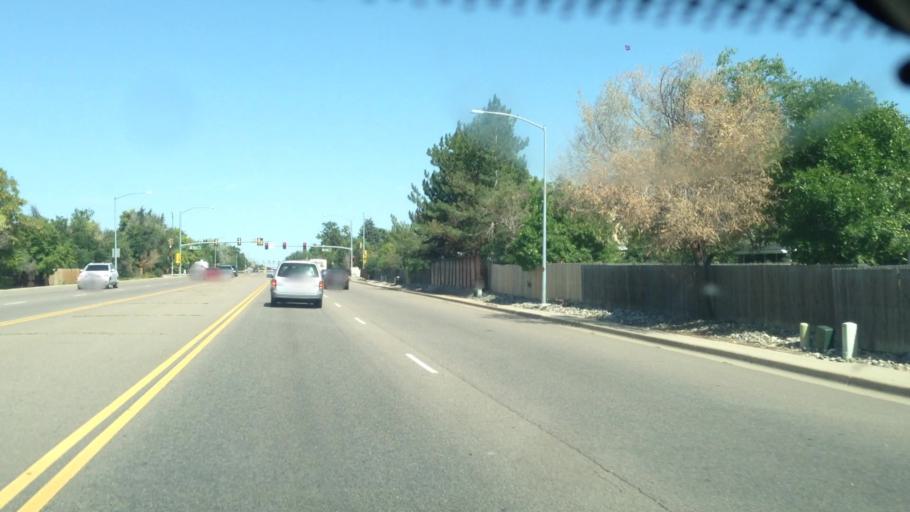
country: US
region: Colorado
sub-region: Adams County
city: Aurora
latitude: 39.7256
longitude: -104.8591
